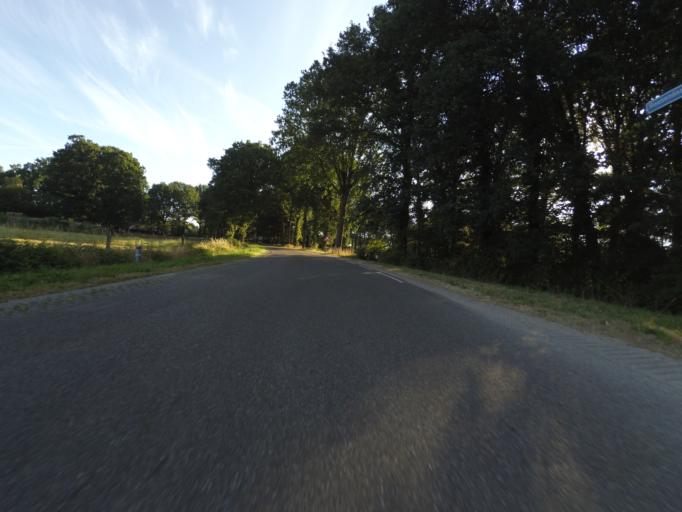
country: NL
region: Gelderland
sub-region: Gemeente Putten
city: Putten
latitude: 52.2470
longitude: 5.5896
